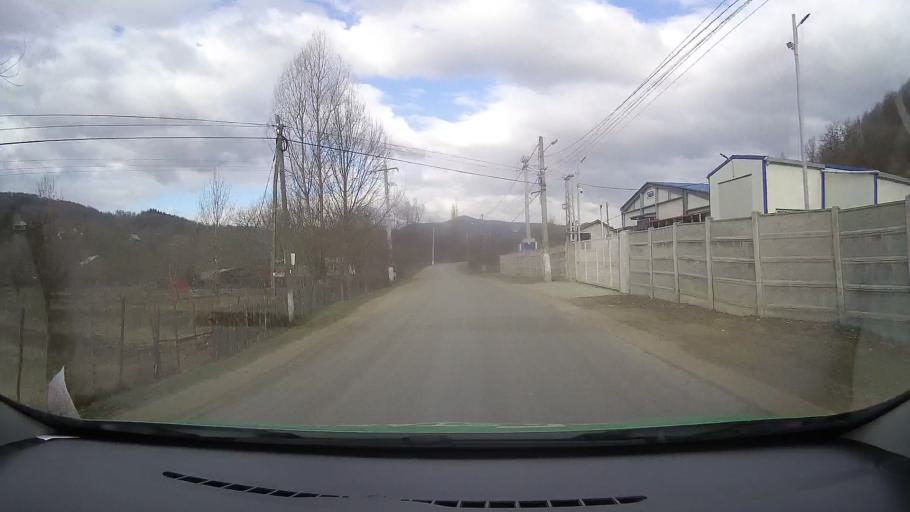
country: RO
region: Prahova
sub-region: Comuna Provita de Jos
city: Provita de Jos
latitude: 45.1244
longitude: 25.6555
